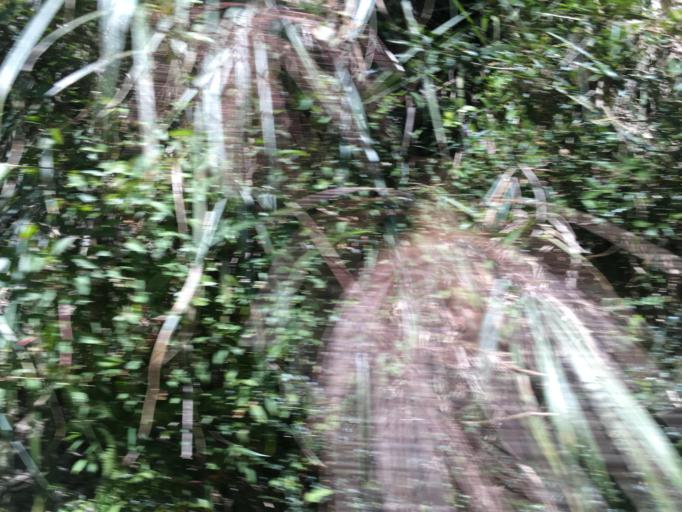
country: TW
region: Taiwan
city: Daxi
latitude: 24.5782
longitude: 121.4117
